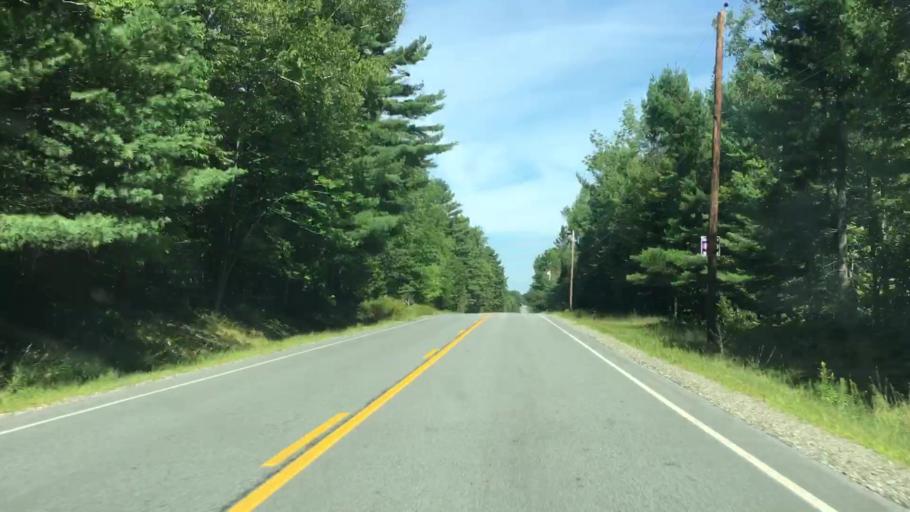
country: US
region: Maine
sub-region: Penobscot County
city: Howland
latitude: 45.2198
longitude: -68.7879
